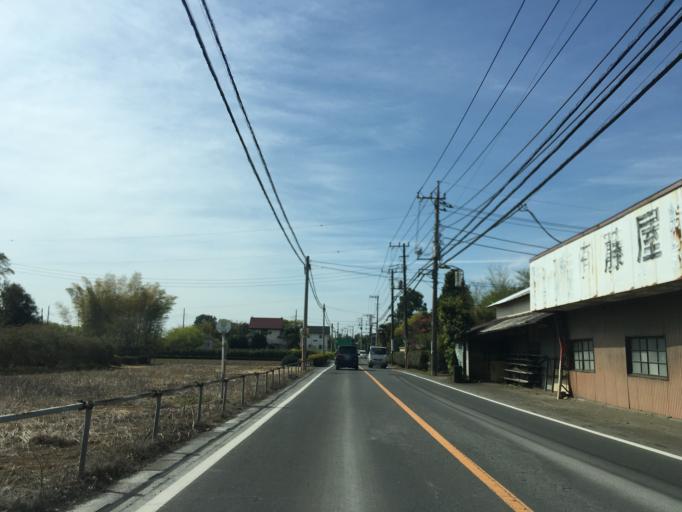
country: JP
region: Saitama
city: Ageoshimo
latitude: 35.9799
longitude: 139.6334
